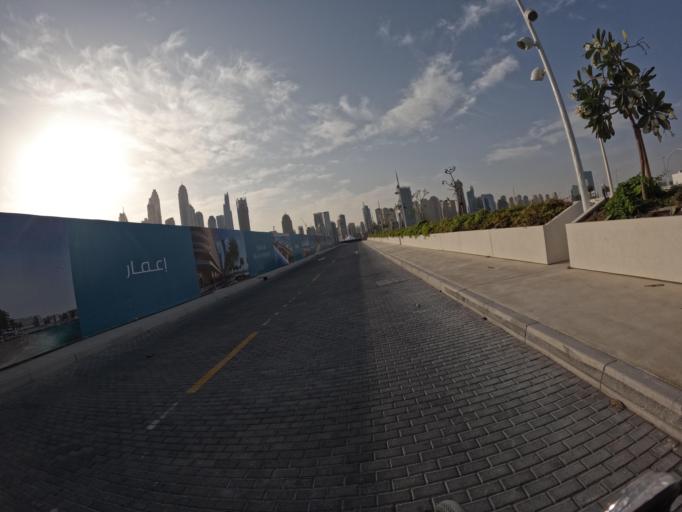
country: AE
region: Dubai
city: Dubai
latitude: 25.0956
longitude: 55.1354
